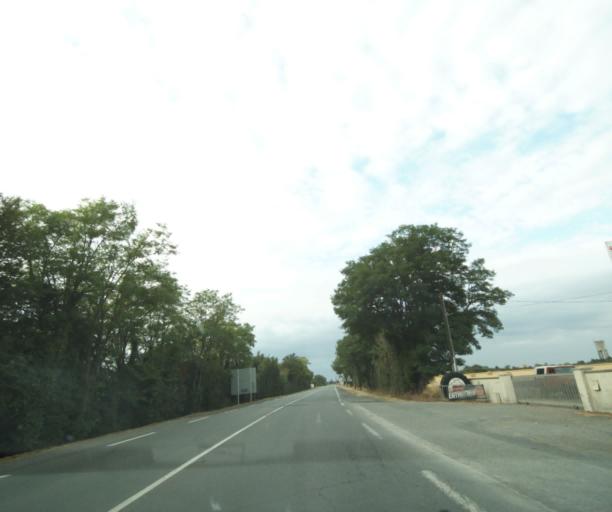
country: FR
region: Poitou-Charentes
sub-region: Departement de la Charente-Maritime
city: Marans
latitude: 46.2967
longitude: -0.9911
